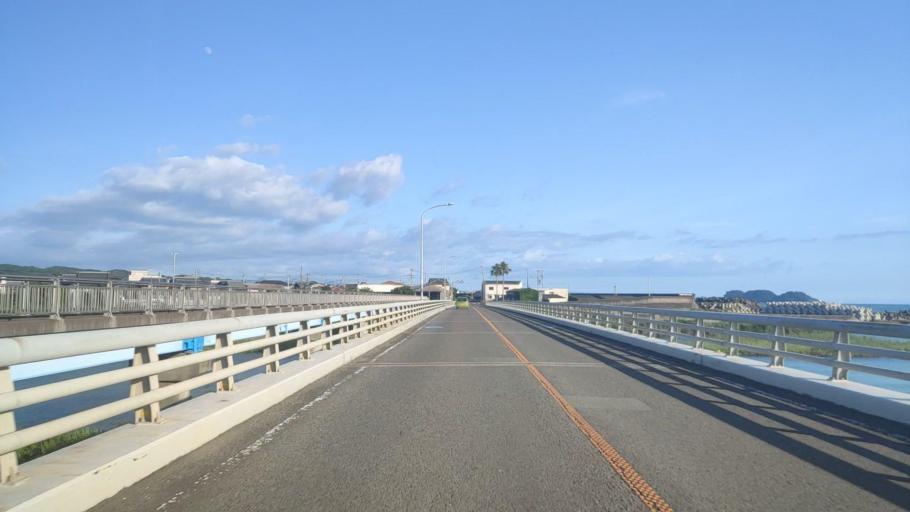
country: JP
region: Wakayama
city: Tanabe
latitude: 33.7708
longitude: 135.3143
